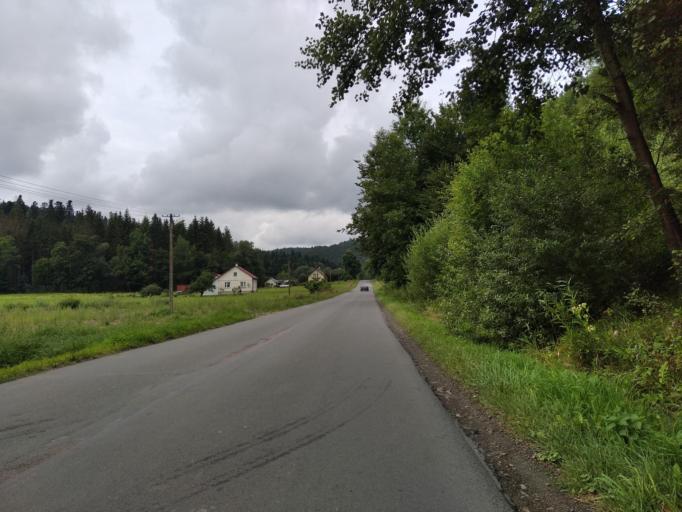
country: PL
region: Subcarpathian Voivodeship
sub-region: Powiat przemyski
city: Bircza
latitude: 49.6904
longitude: 22.4388
